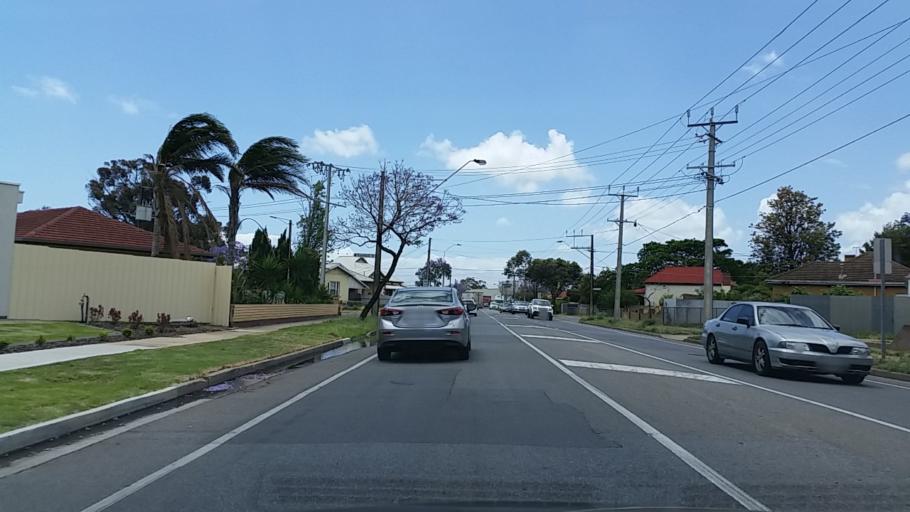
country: AU
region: South Australia
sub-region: Charles Sturt
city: Woodville
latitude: -34.8796
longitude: 138.5502
